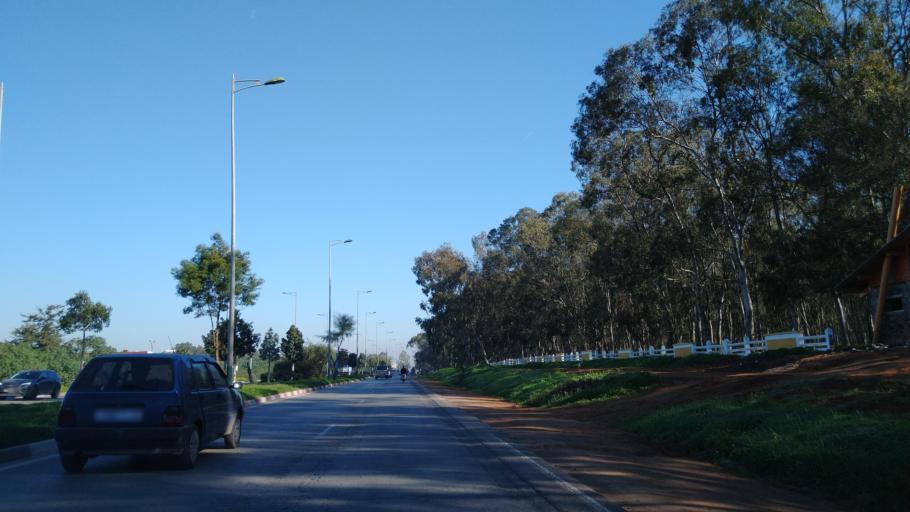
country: MA
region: Rabat-Sale-Zemmour-Zaer
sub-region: Skhirate-Temara
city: Temara
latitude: 33.9373
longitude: -6.8823
